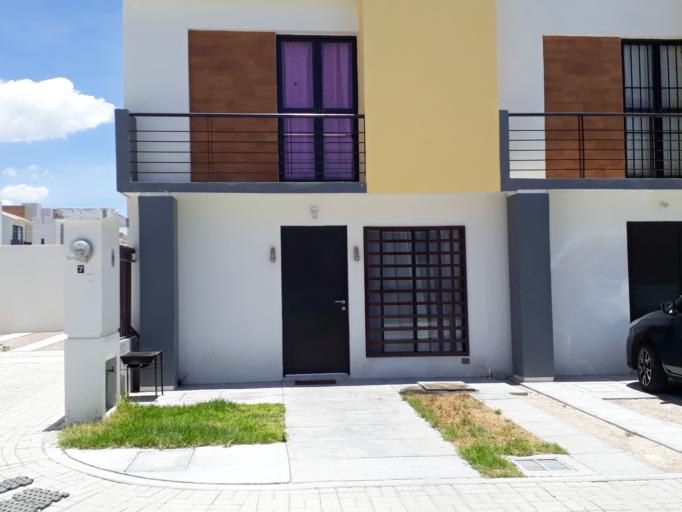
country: MX
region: Aguascalientes
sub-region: Aguascalientes
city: San Sebastian [Fraccionamiento]
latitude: 21.8060
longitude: -102.3017
